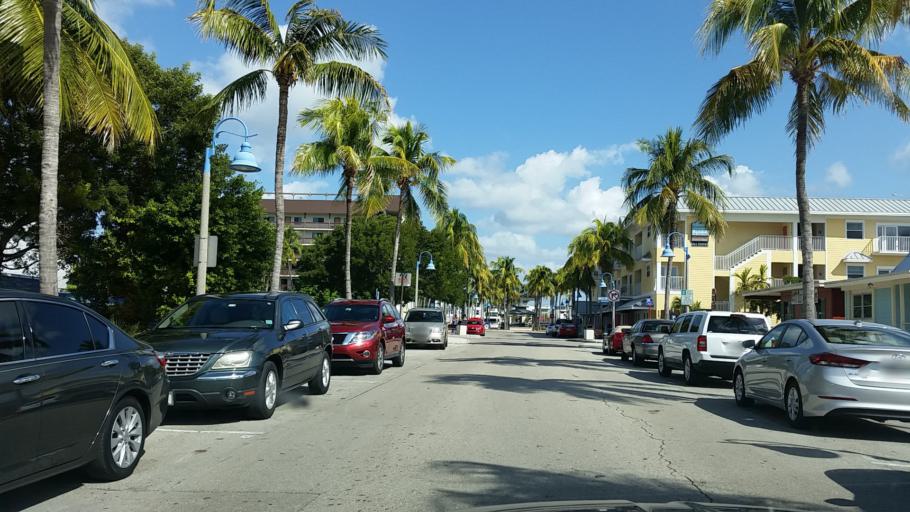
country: US
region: Florida
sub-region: Lee County
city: Fort Myers Beach
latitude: 26.4554
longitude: -81.9551
